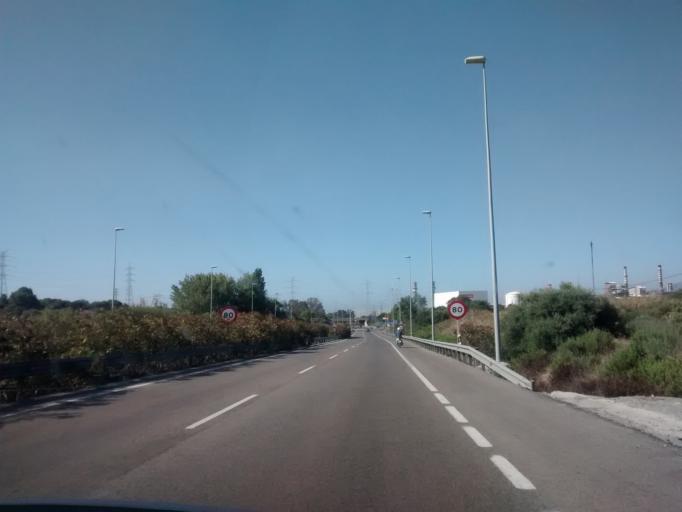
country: ES
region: Andalusia
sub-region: Provincia de Cadiz
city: San Roque
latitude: 36.1945
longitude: -5.3841
